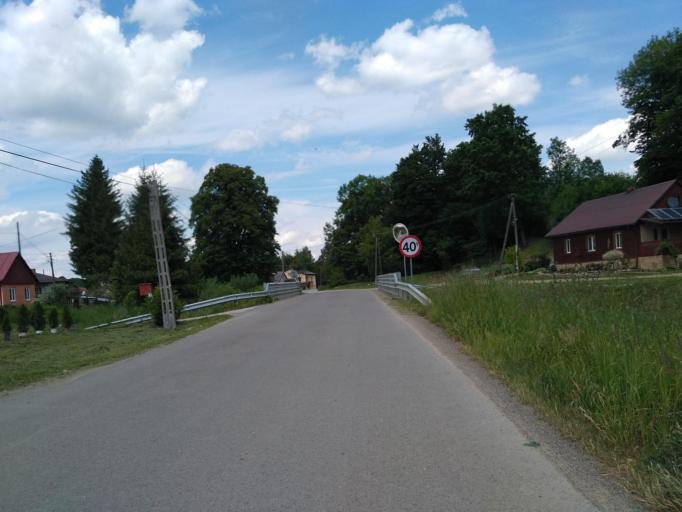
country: PL
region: Subcarpathian Voivodeship
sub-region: Powiat krosnienski
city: Chorkowka
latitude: 49.5947
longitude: 21.6220
